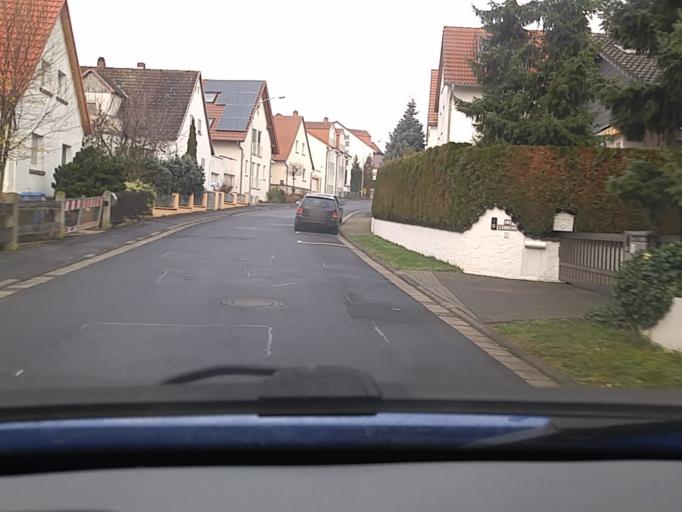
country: DE
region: Hesse
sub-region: Regierungsbezirk Darmstadt
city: Bad Nauheim
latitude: 50.3770
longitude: 8.7655
